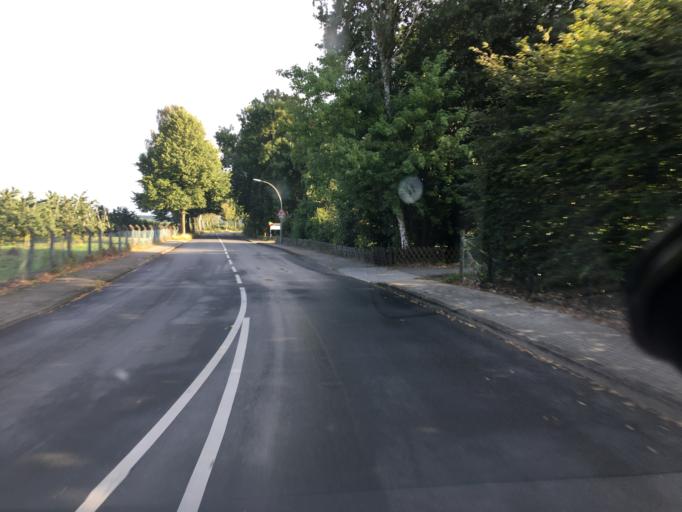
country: DE
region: Hamburg
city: Altona
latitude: 53.5011
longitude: 9.8774
